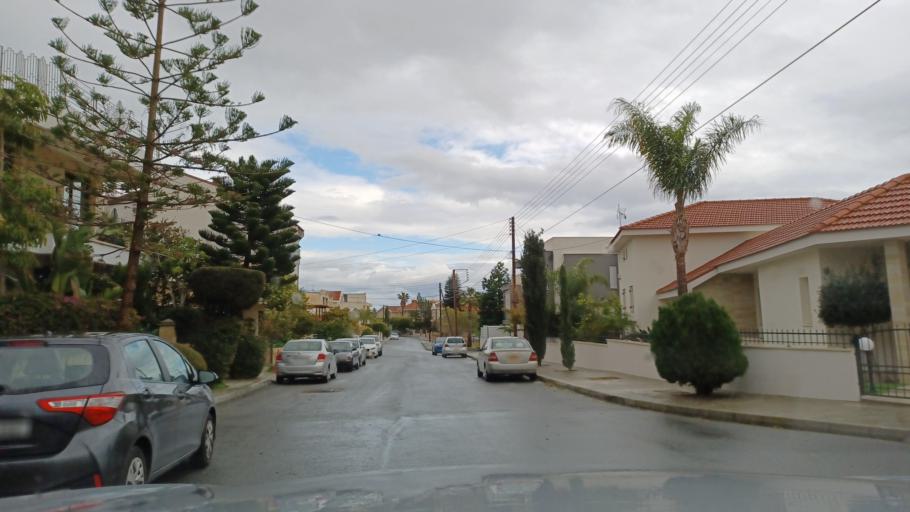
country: CY
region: Limassol
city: Pano Polemidia
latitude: 34.7079
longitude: 33.0033
